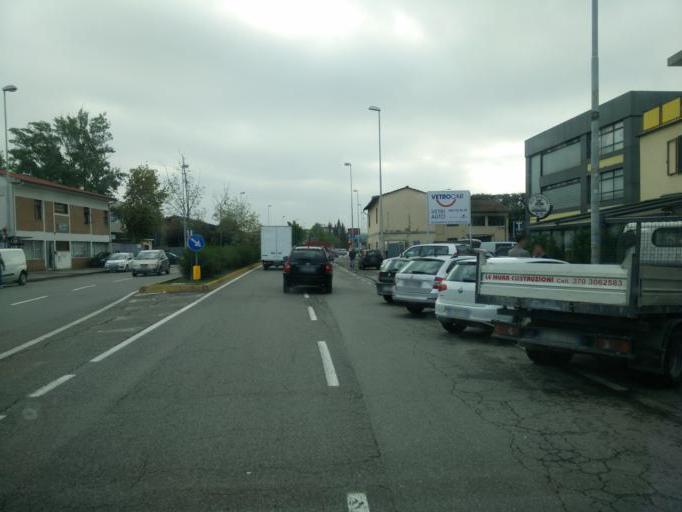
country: IT
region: Tuscany
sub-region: Province of Florence
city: Mantignano-Ugnano
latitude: 43.8022
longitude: 11.1888
